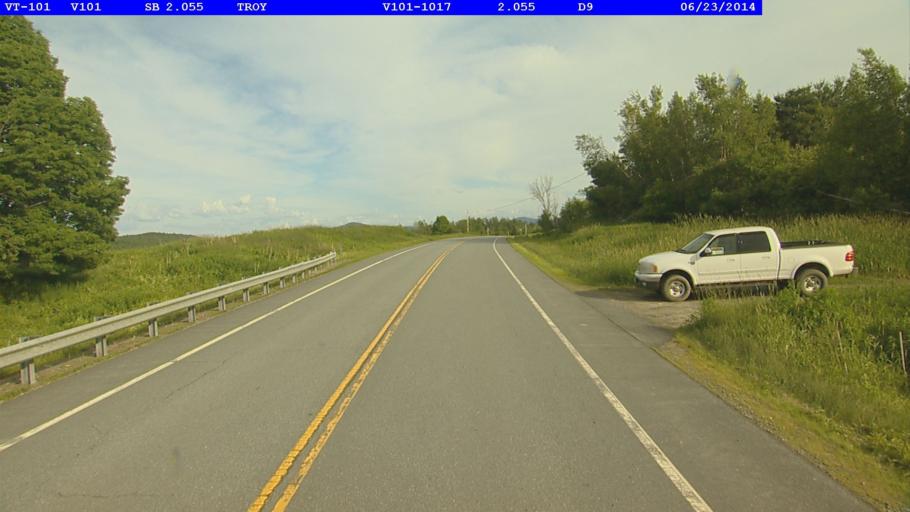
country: US
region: Vermont
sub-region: Orleans County
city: Newport
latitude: 44.9324
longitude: -72.4099
